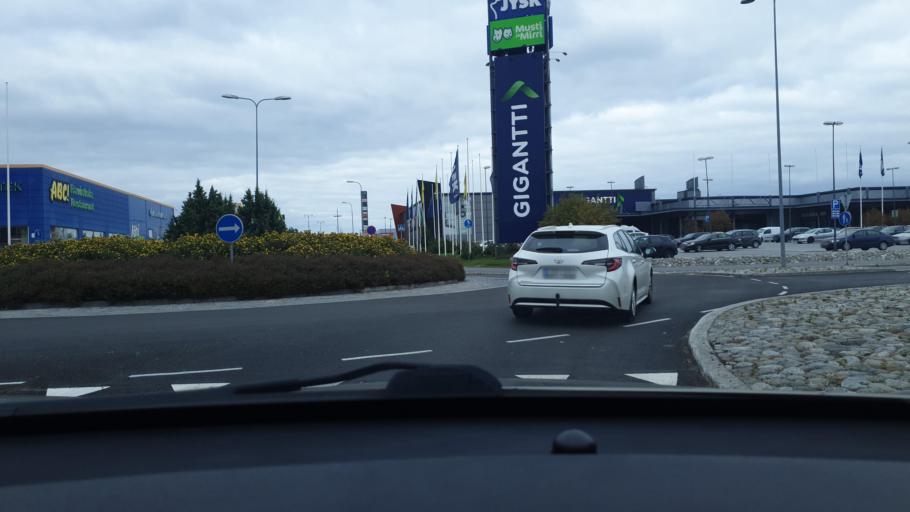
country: FI
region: Ostrobothnia
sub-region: Vaasa
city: Korsholm
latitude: 63.1103
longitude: 21.6515
